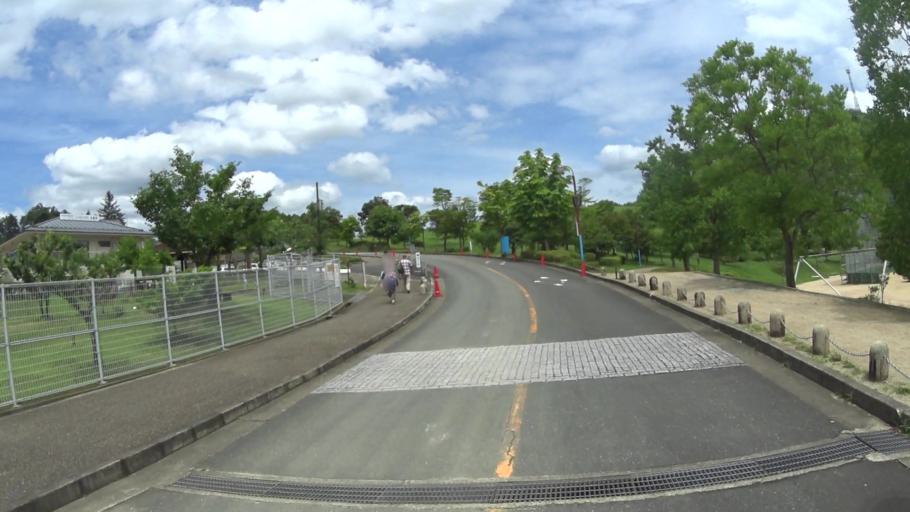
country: JP
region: Kyoto
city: Ayabe
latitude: 35.1629
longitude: 135.4158
